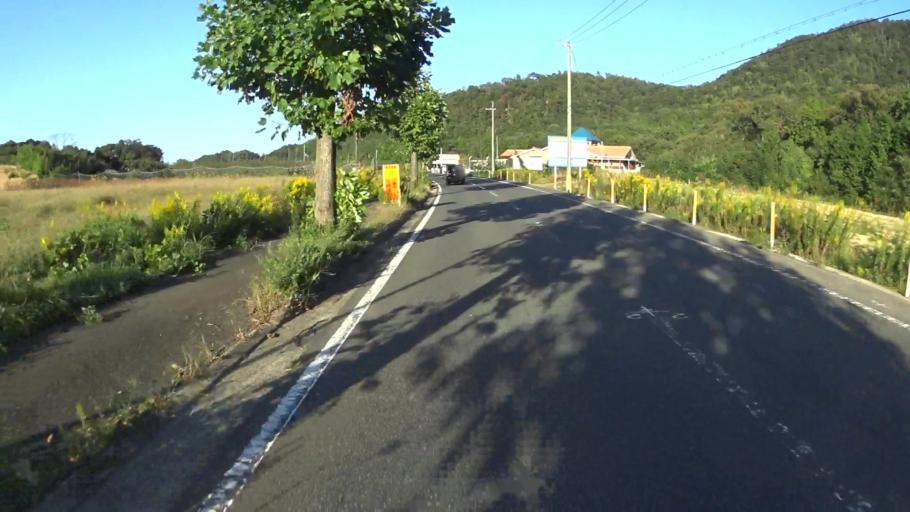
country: JP
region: Hyogo
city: Toyooka
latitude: 35.6205
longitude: 134.9266
